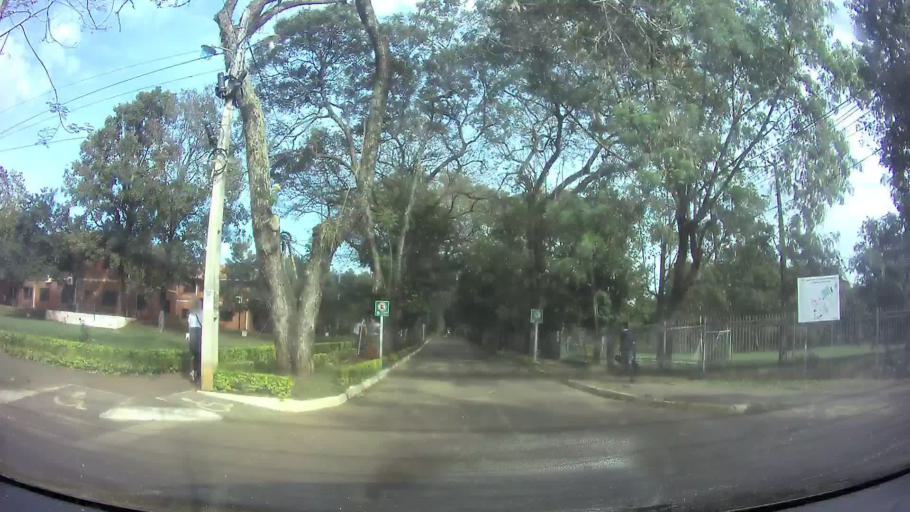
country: PY
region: Central
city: Fernando de la Mora
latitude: -25.3332
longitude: -57.5178
